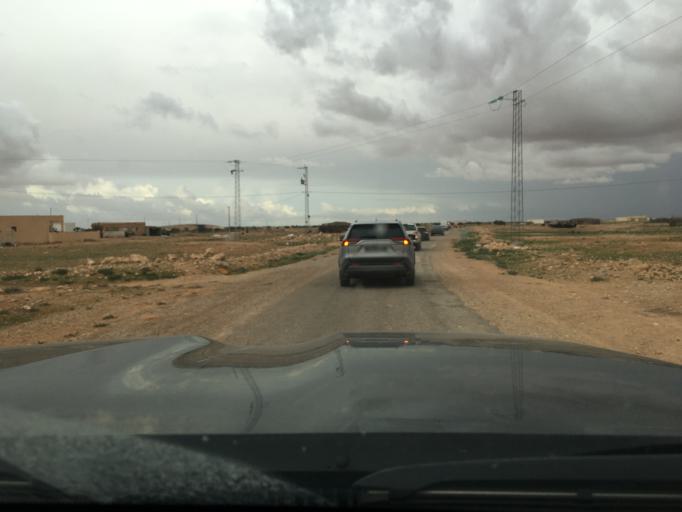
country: TN
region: Madanin
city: Medenine
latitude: 33.2920
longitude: 10.6070
